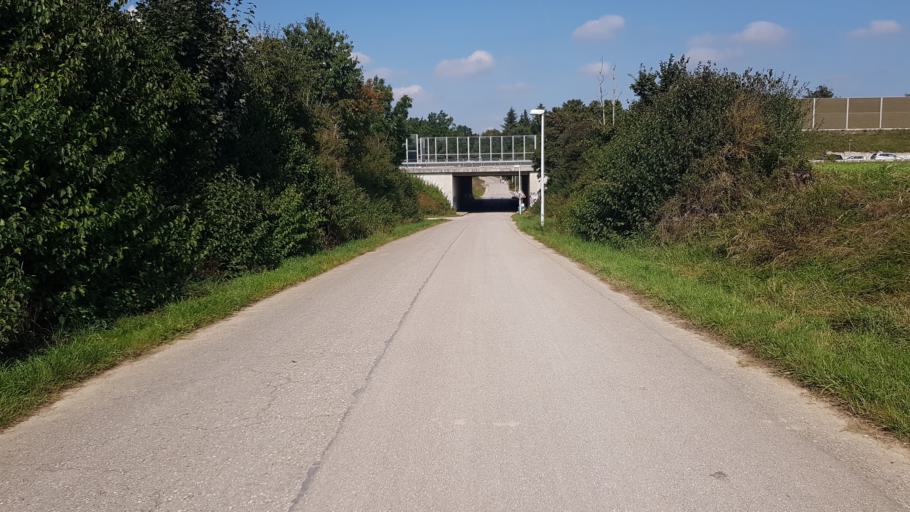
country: DE
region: Bavaria
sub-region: Upper Bavaria
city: Gilching
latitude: 48.0938
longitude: 11.3024
